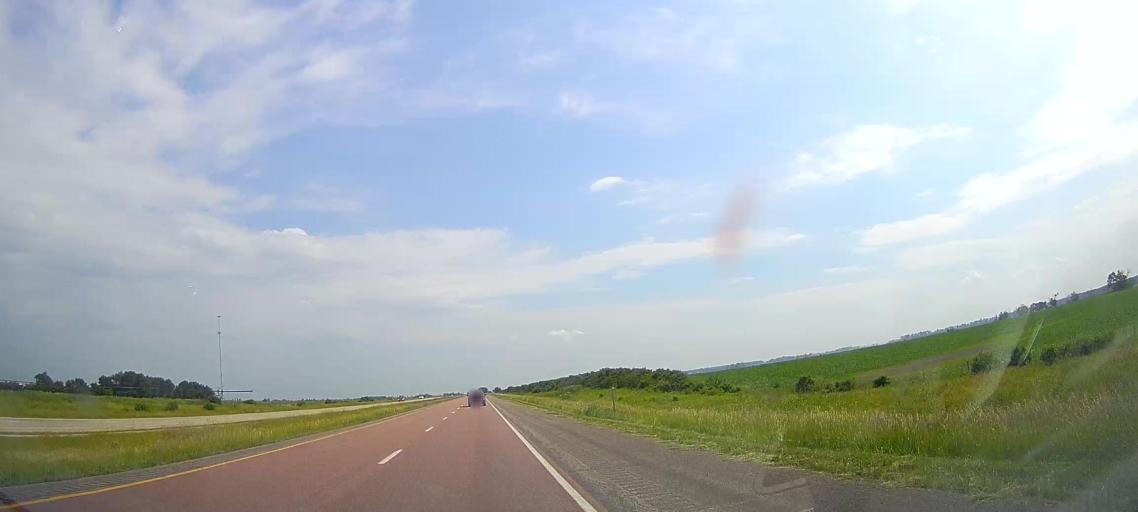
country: US
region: Iowa
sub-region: Monona County
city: Onawa
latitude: 41.9604
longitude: -96.1029
